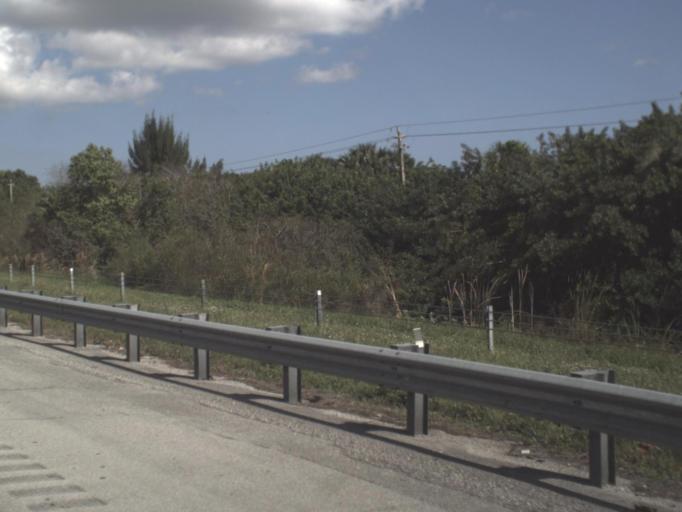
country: US
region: Florida
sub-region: Palm Beach County
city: Palm Beach Gardens
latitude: 26.8187
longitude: -80.1307
